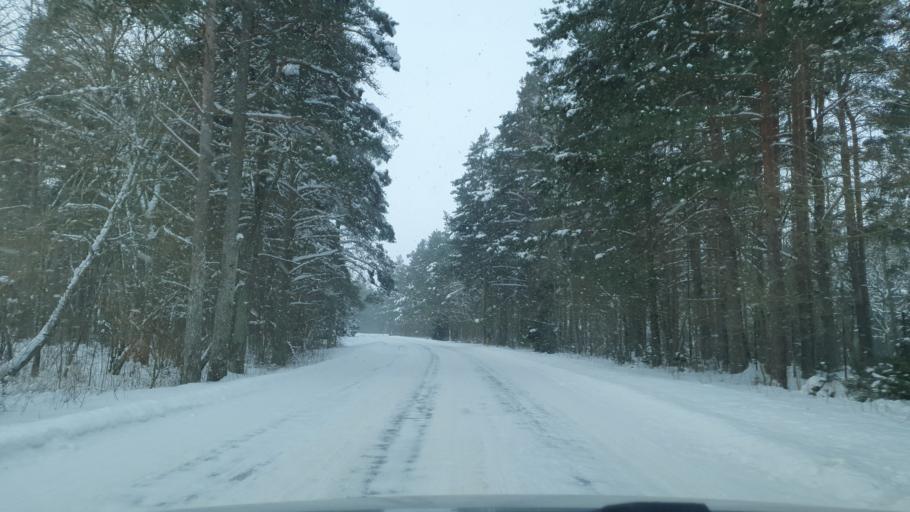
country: EE
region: Harju
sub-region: Kuusalu vald
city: Kuusalu
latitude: 59.4853
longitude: 25.3482
